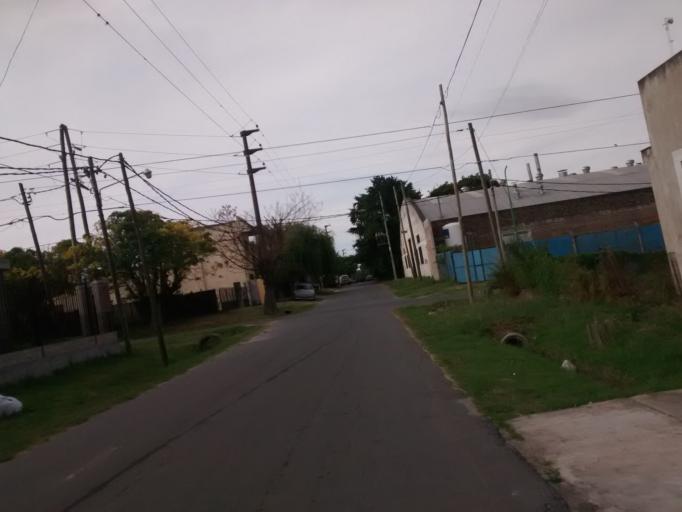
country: AR
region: Buenos Aires
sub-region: Partido de La Plata
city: La Plata
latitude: -34.8552
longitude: -58.0818
